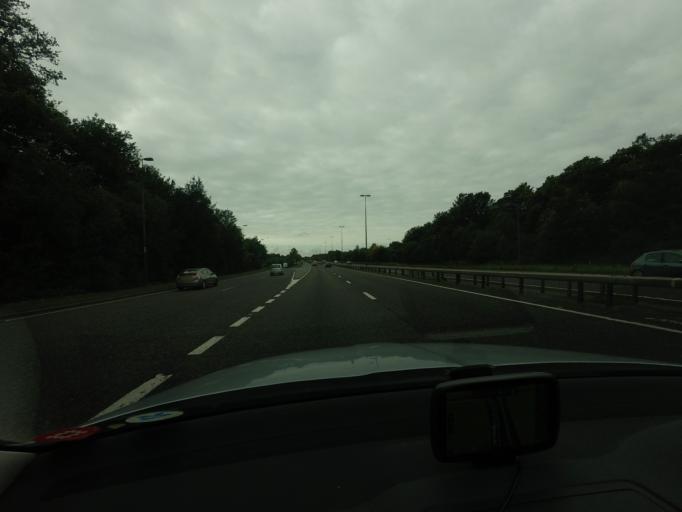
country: GB
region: England
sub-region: Surrey
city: Byfleet
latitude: 51.3251
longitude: -0.4475
